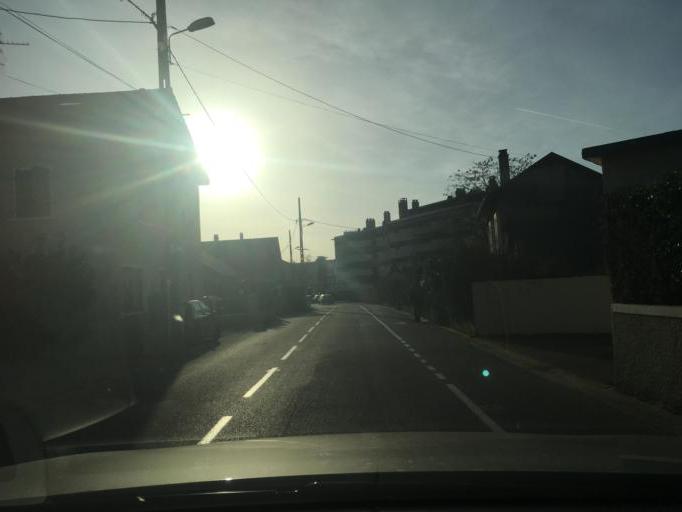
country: FR
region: Rhone-Alpes
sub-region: Departement de la Haute-Savoie
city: Gaillard
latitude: 46.1931
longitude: 6.2187
